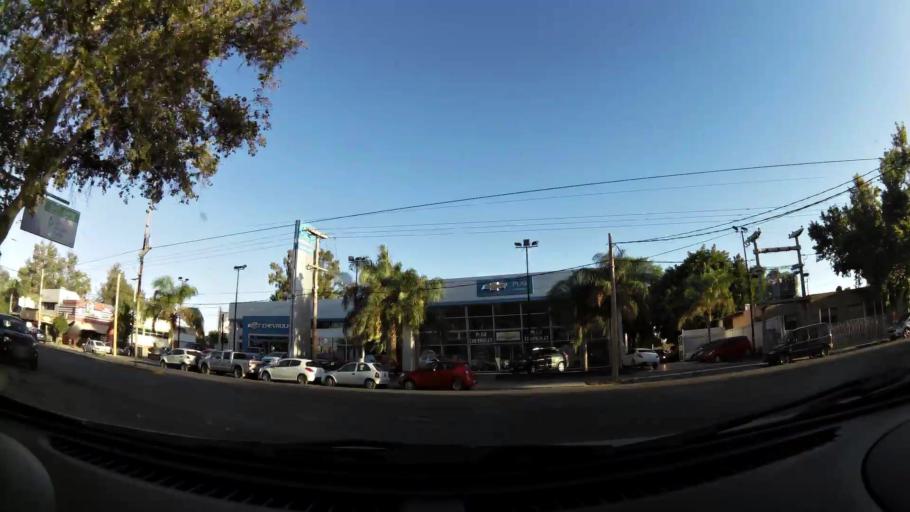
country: AR
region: San Juan
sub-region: Departamento de Santa Lucia
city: Santa Lucia
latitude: -31.5417
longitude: -68.5094
